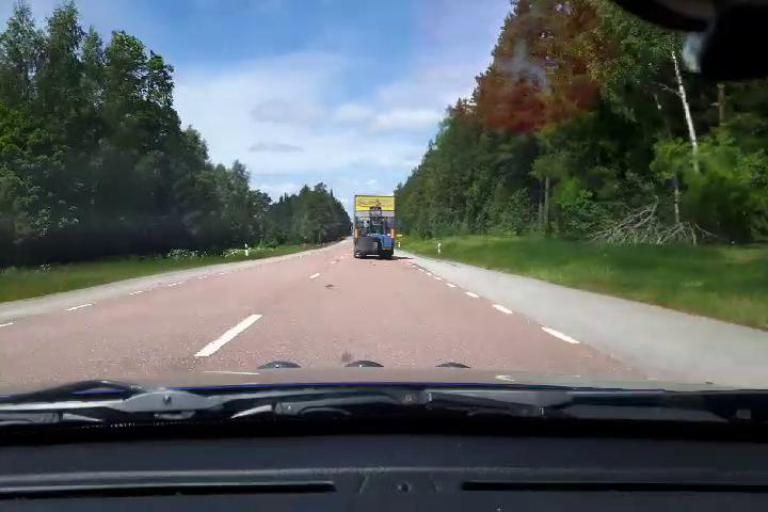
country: SE
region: Uppsala
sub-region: Osthammars Kommun
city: Bjorklinge
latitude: 60.1345
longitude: 17.5078
